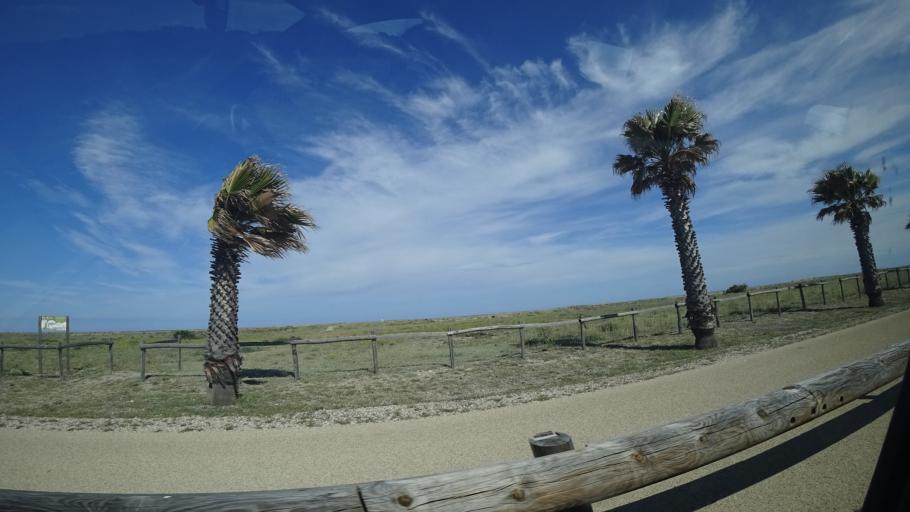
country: FR
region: Languedoc-Roussillon
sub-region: Departement des Pyrenees-Orientales
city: Le Barcares
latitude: 42.8172
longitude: 3.0383
